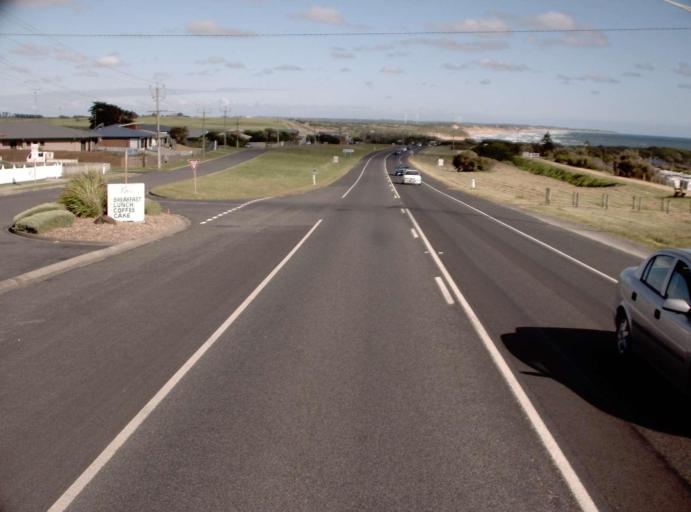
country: AU
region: Victoria
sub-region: Bass Coast
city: North Wonthaggi
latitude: -38.5498
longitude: 145.4763
